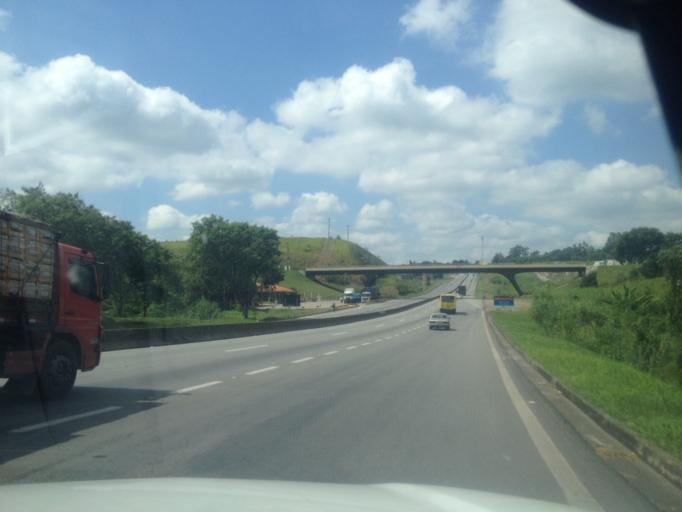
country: BR
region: Rio de Janeiro
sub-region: Volta Redonda
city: Volta Redonda
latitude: -22.5888
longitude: -44.0837
